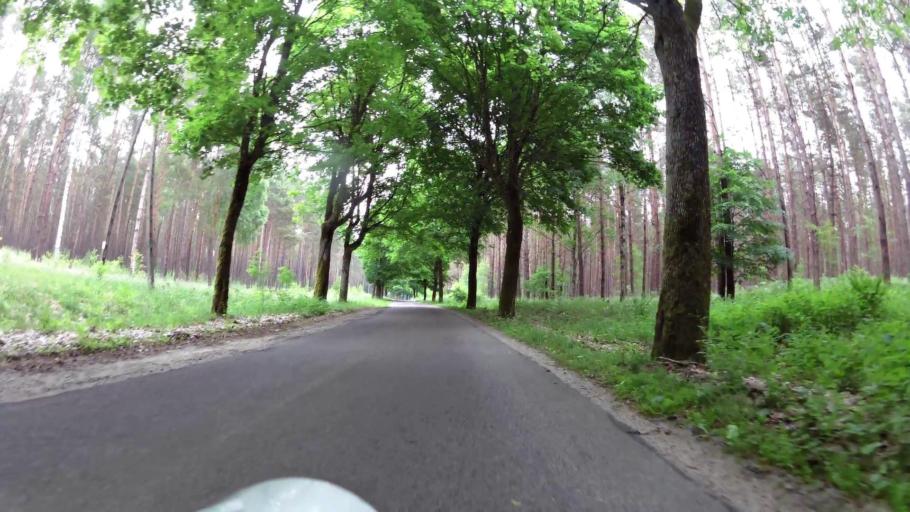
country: PL
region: West Pomeranian Voivodeship
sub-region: Powiat szczecinecki
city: Bialy Bor
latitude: 53.8675
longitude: 16.7733
